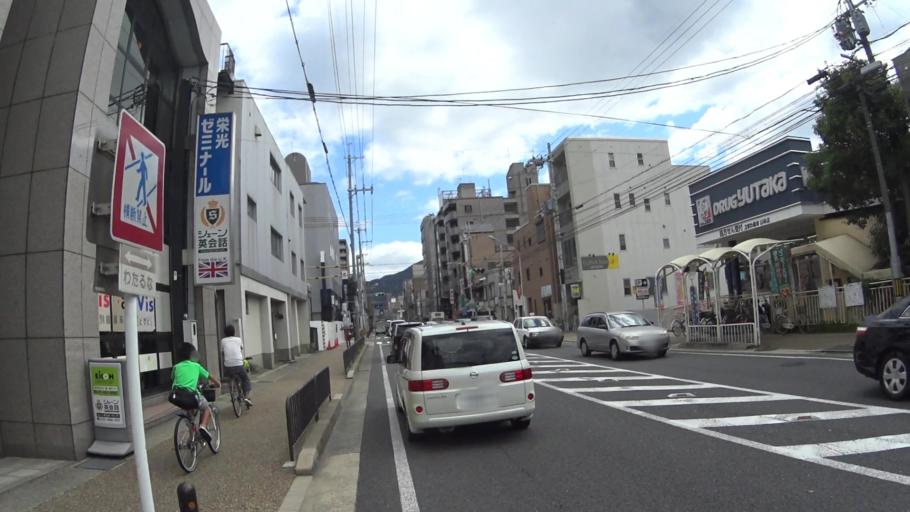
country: JP
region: Shiga Prefecture
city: Otsu-shi
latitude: 34.9898
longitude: 135.8153
